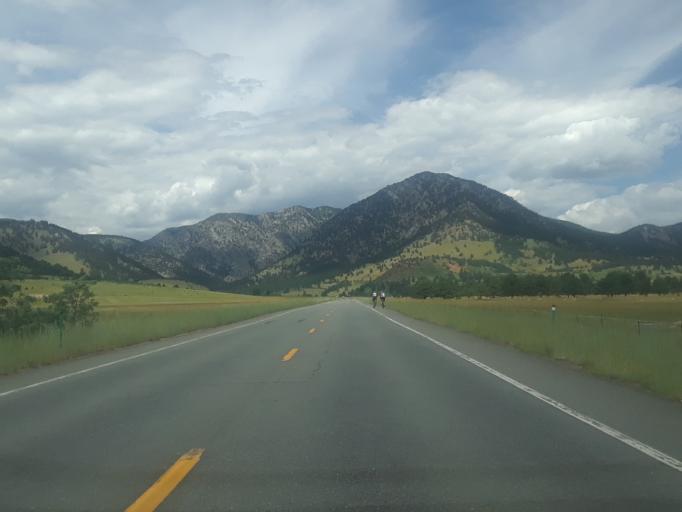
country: US
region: Colorado
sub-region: Jefferson County
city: Golden
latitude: 39.8700
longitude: -105.2574
